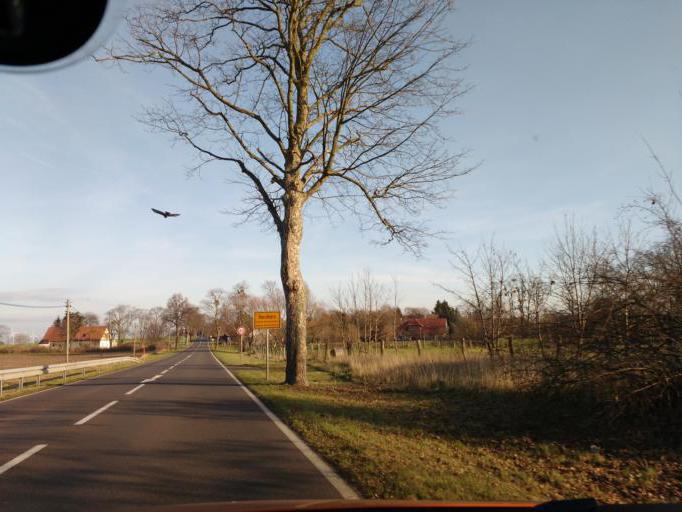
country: DE
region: Brandenburg
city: Protzel
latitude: 52.6562
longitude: 14.0320
